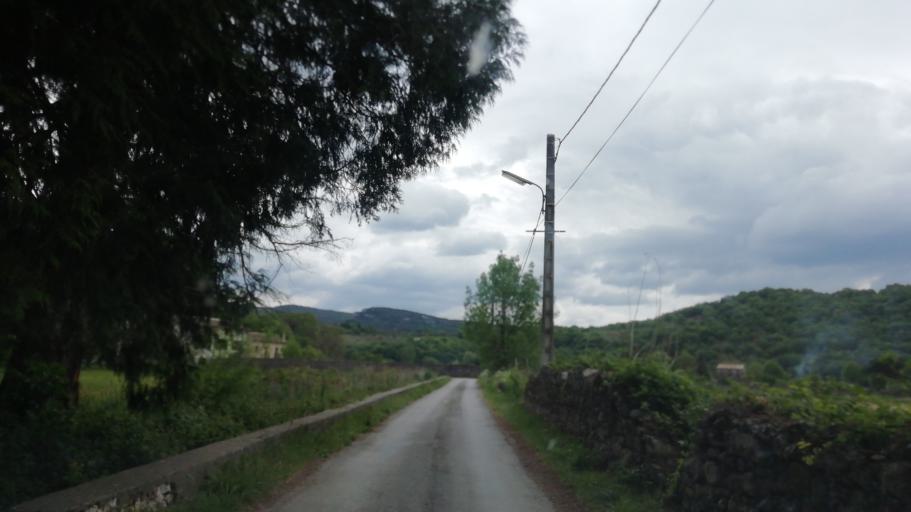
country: FR
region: Languedoc-Roussillon
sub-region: Departement de l'Herault
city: Cazilhac
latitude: 43.9234
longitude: 3.7090
